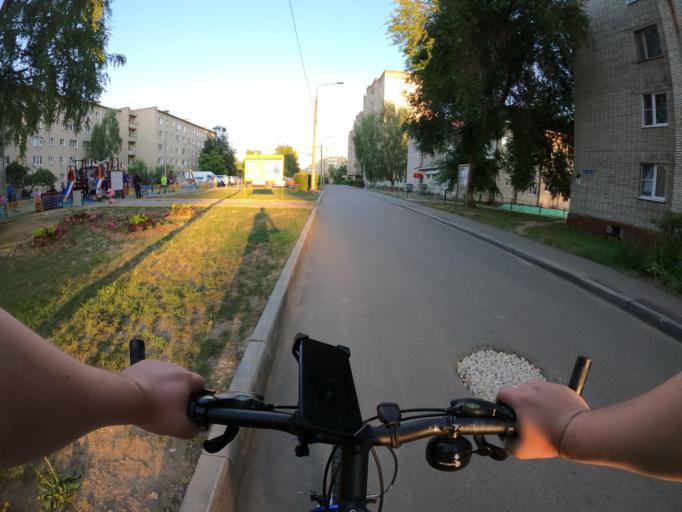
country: RU
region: Moskovskaya
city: Beloozerskiy
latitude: 55.4617
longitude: 38.4341
